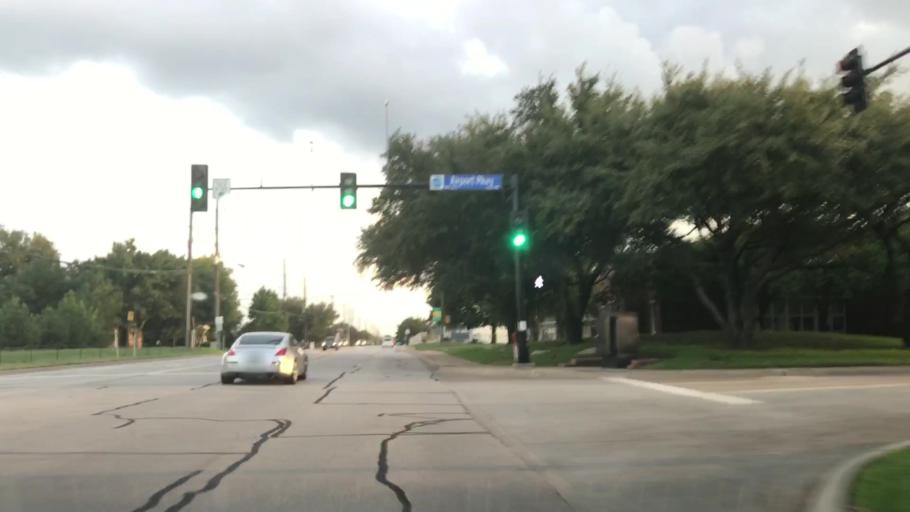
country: US
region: Texas
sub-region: Dallas County
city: Addison
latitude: 32.9662
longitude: -96.8299
